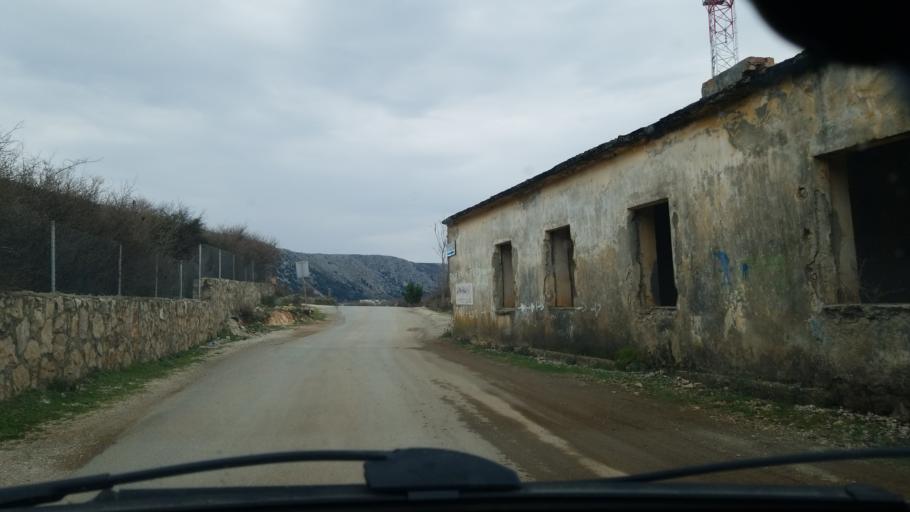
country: AL
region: Lezhe
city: Shengjin
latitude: 41.8109
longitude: 19.5824
